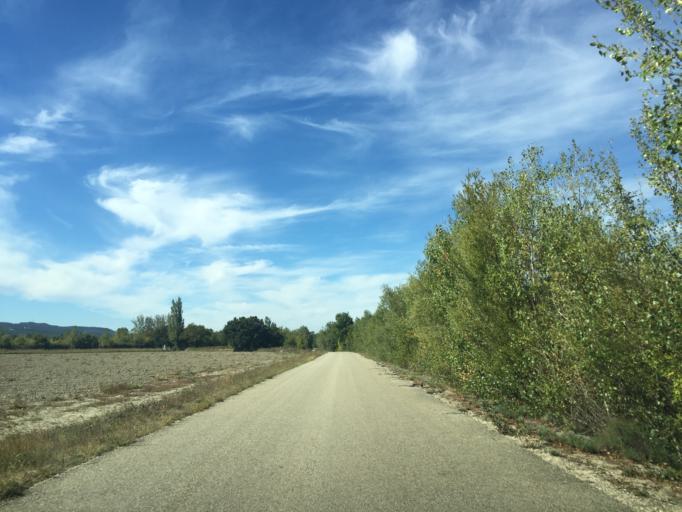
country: FR
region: Provence-Alpes-Cote d'Azur
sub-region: Departement du Vaucluse
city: Piolenc
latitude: 44.1585
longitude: 4.7410
